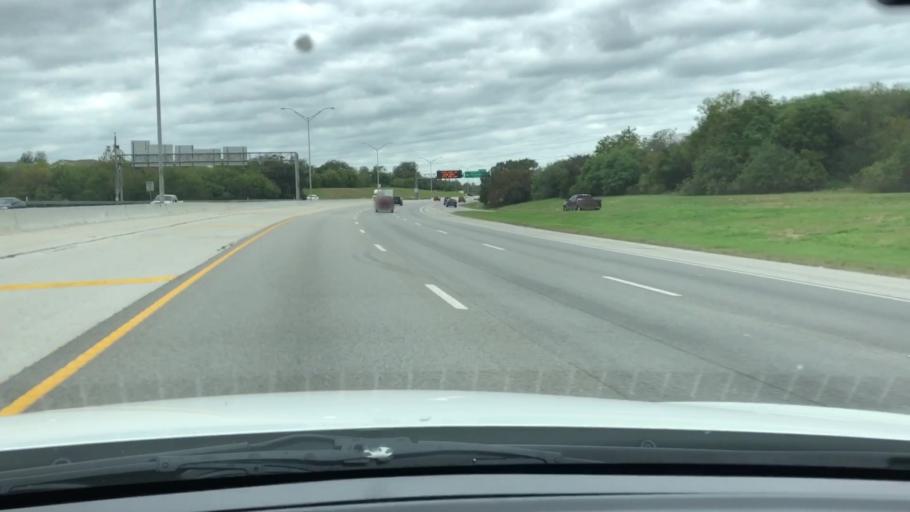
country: US
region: Texas
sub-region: Bexar County
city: San Antonio
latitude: 29.4022
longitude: -98.4458
